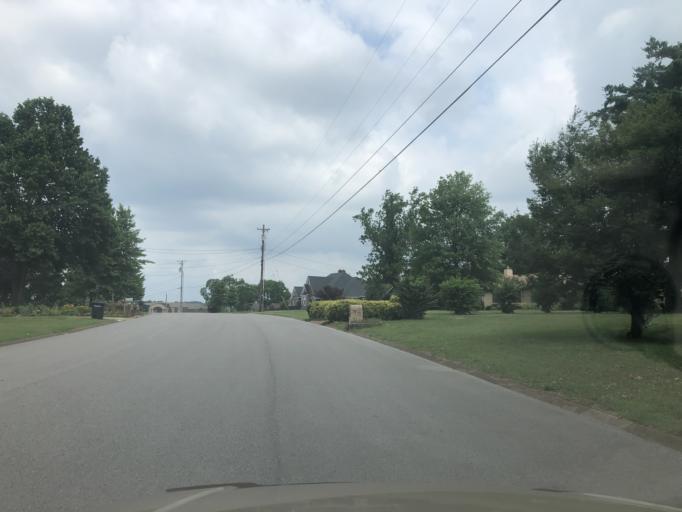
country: US
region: Tennessee
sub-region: Davidson County
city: Lakewood
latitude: 36.2415
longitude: -86.6170
